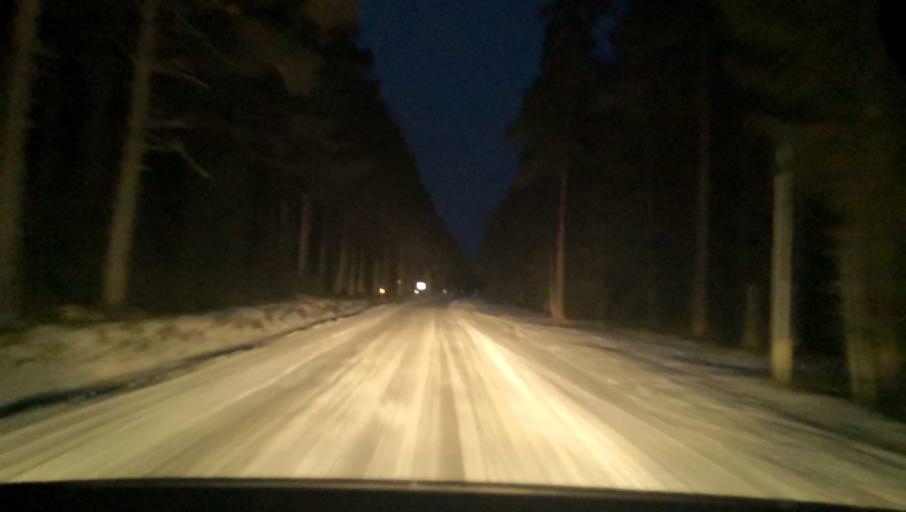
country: SE
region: Uppsala
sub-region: Heby Kommun
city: Tarnsjo
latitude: 60.2805
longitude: 16.8038
